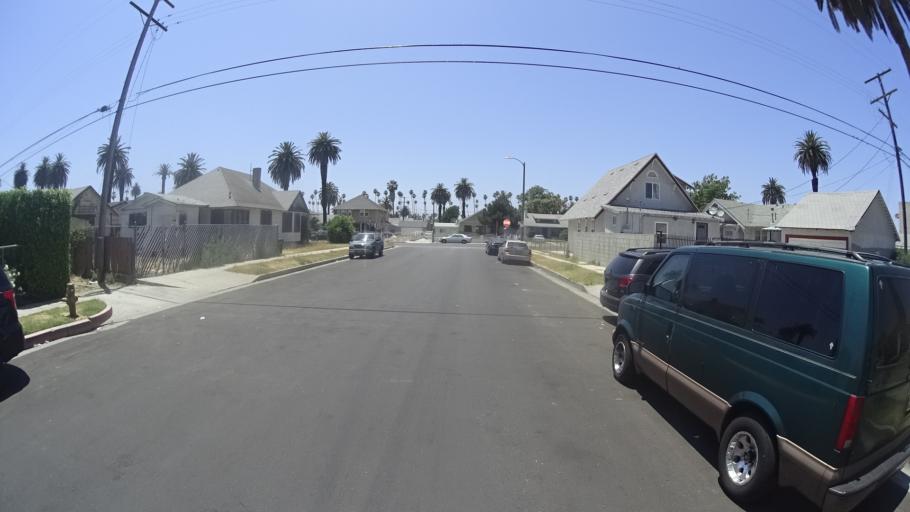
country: US
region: California
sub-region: Los Angeles County
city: View Park-Windsor Hills
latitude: 33.9980
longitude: -118.3132
